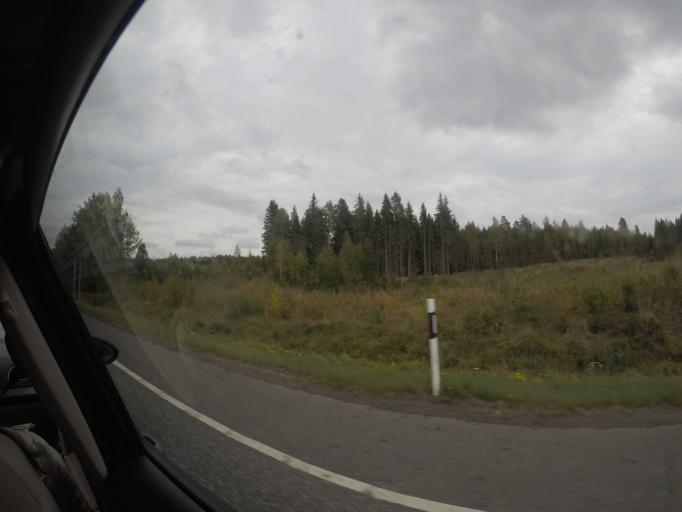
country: FI
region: Haeme
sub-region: Haemeenlinna
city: Parola
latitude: 61.1779
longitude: 24.4125
